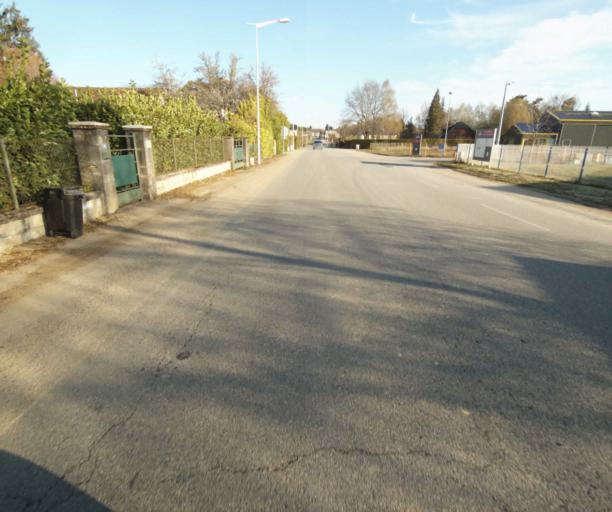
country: FR
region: Limousin
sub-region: Departement de la Correze
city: Correze
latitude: 45.3352
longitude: 1.8775
